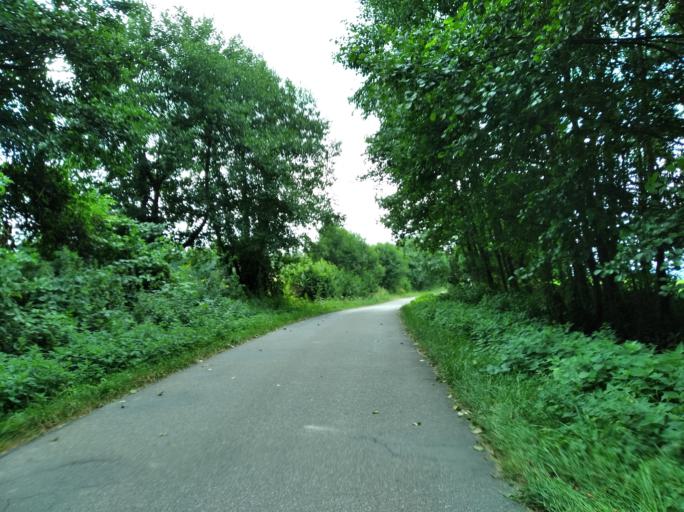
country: PL
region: Subcarpathian Voivodeship
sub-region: Powiat krosnienski
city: Leki
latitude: 49.8174
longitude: 21.6645
